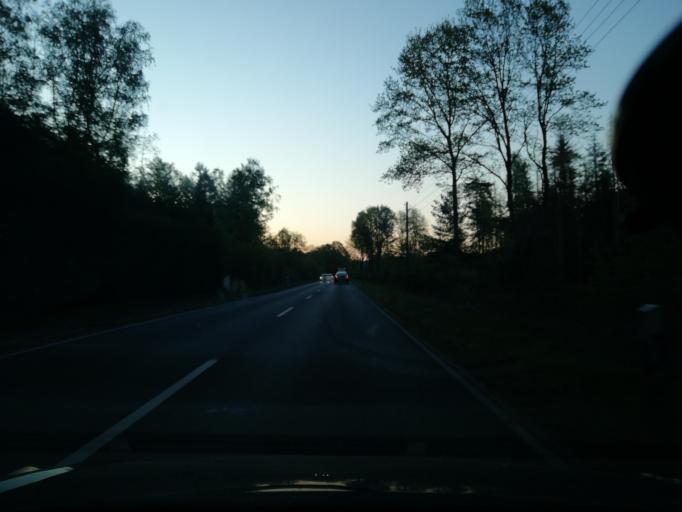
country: DE
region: North Rhine-Westphalia
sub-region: Regierungsbezirk Detmold
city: Verl
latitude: 51.9372
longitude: 8.4980
